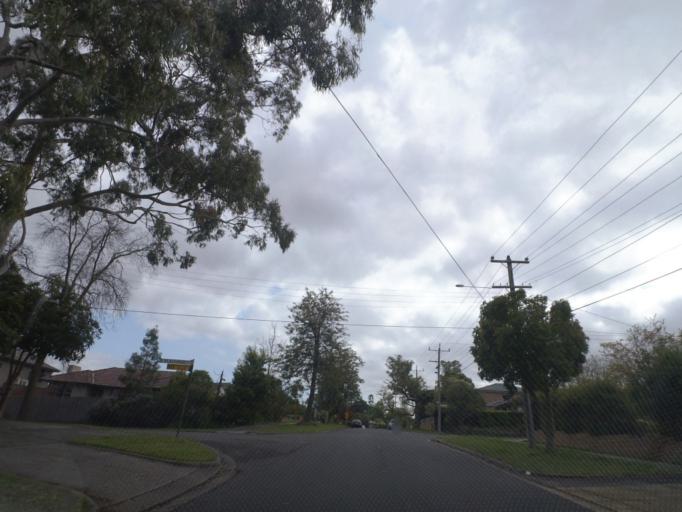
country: AU
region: Victoria
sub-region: Whitehorse
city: Nunawading
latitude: -37.8110
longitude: 145.1848
